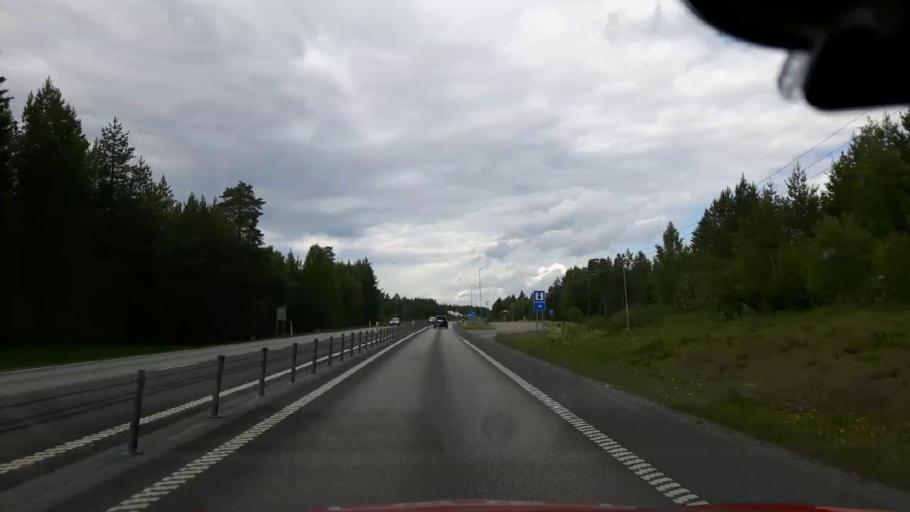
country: SE
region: Jaemtland
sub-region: OEstersunds Kommun
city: Ostersund
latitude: 63.2312
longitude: 14.6129
